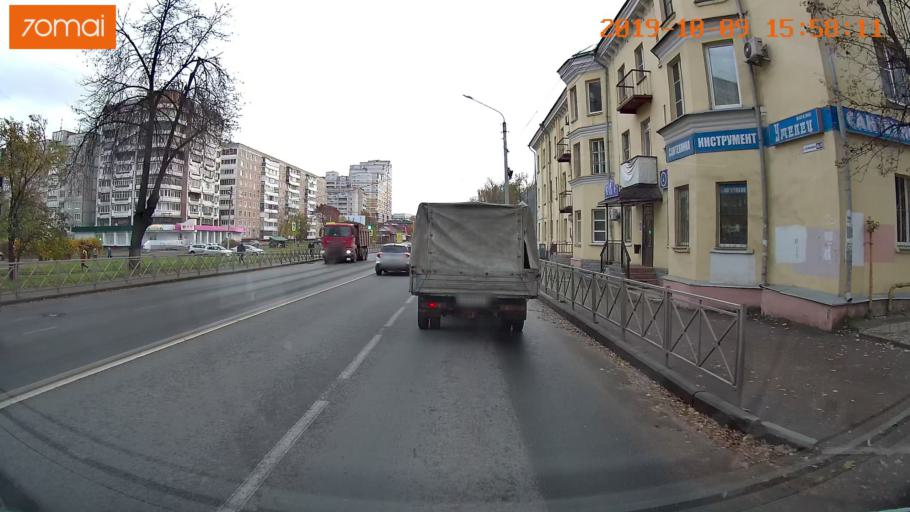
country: RU
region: Kostroma
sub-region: Kostromskoy Rayon
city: Kostroma
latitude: 57.7674
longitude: 40.9509
